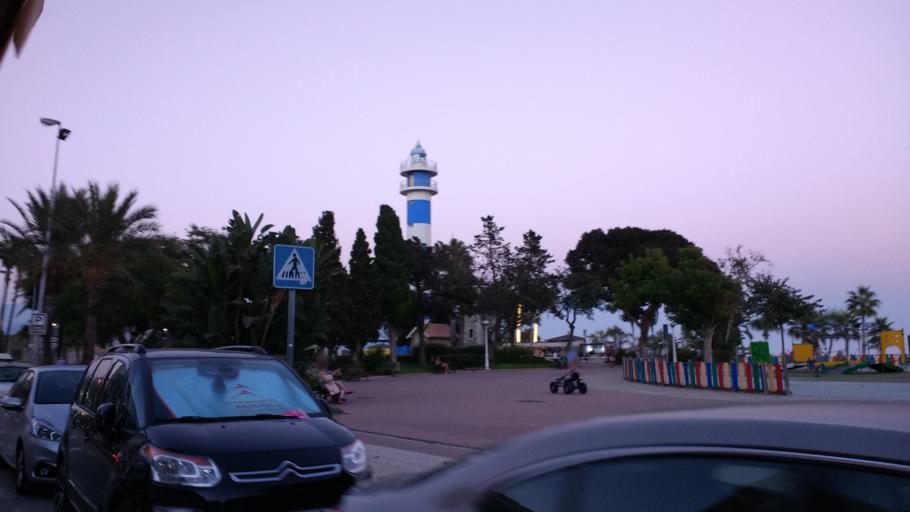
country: ES
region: Andalusia
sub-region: Provincia de Malaga
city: Velez-Malaga
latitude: 36.7348
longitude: -4.0971
